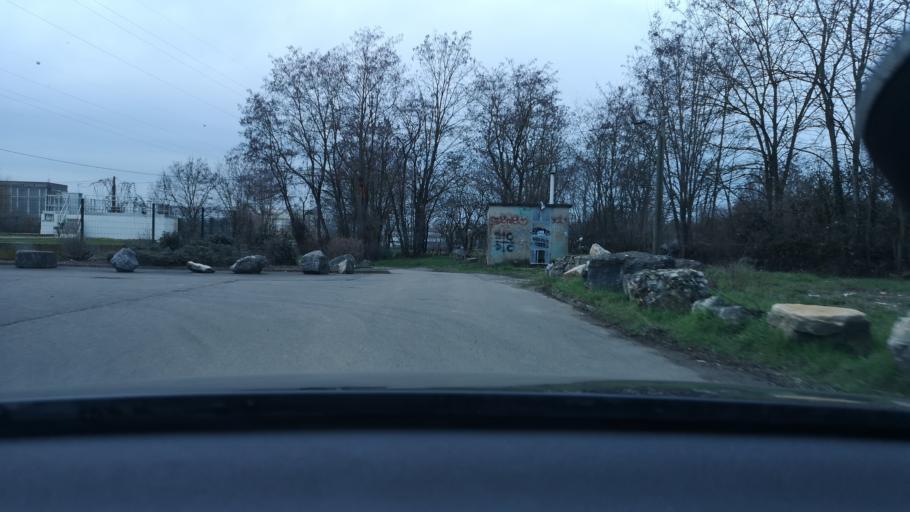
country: FR
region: Bourgogne
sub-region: Departement de Saone-et-Loire
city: Chalon-sur-Saone
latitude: 46.7724
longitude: 4.8485
